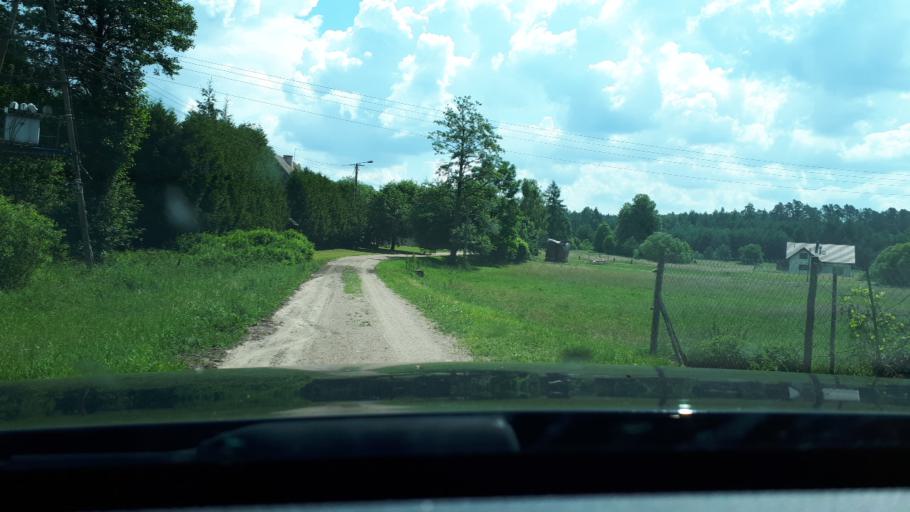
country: PL
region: Podlasie
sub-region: Powiat bialostocki
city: Suprasl
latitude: 53.2446
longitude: 23.3495
